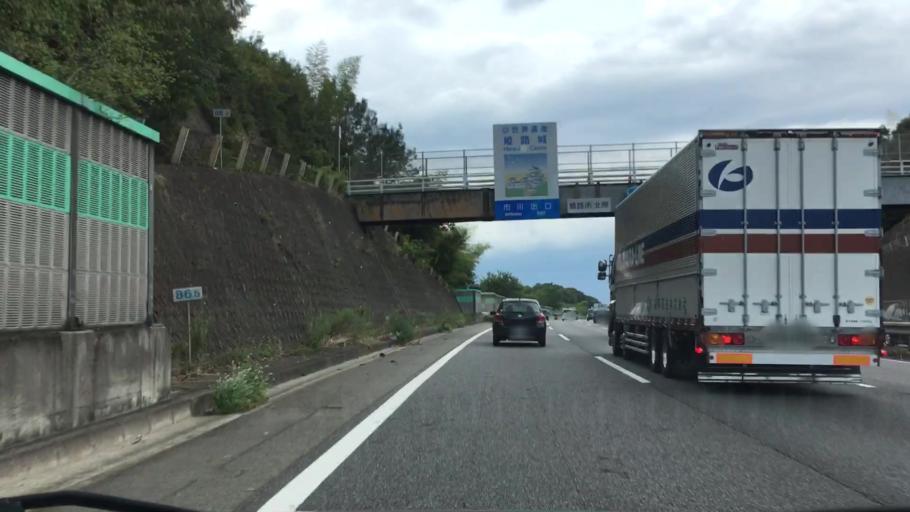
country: JP
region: Hyogo
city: Shirahamacho-usazakiminami
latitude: 34.8001
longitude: 134.7105
